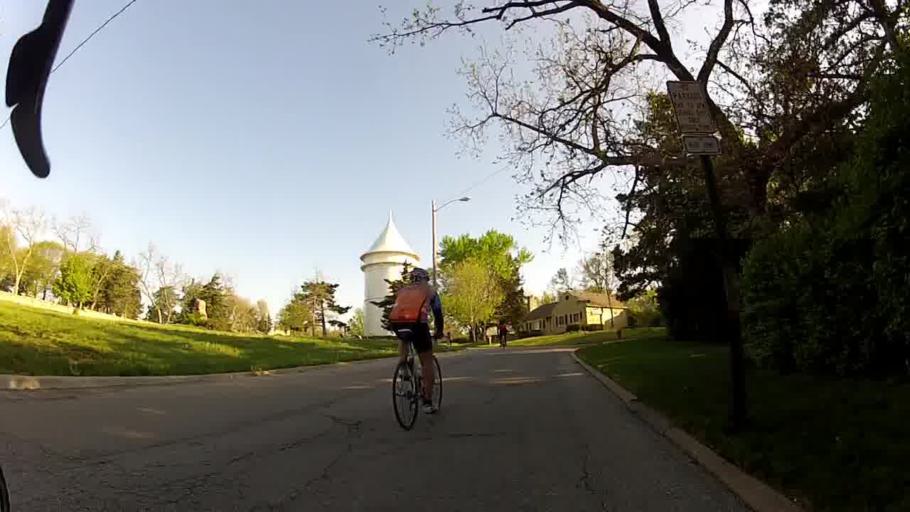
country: US
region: Kansas
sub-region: Riley County
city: Manhattan
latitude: 39.1805
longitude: -96.5881
